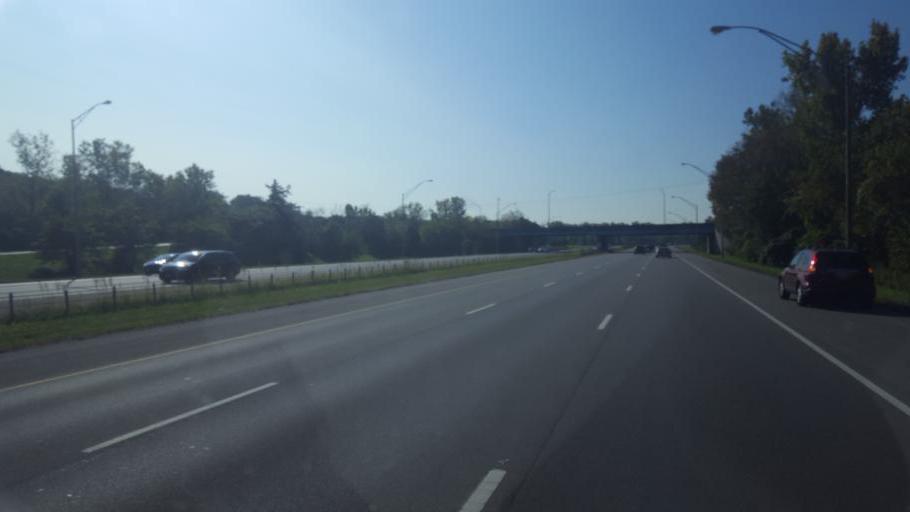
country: US
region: Ohio
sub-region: Franklin County
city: Worthington
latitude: 40.0647
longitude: -83.0326
